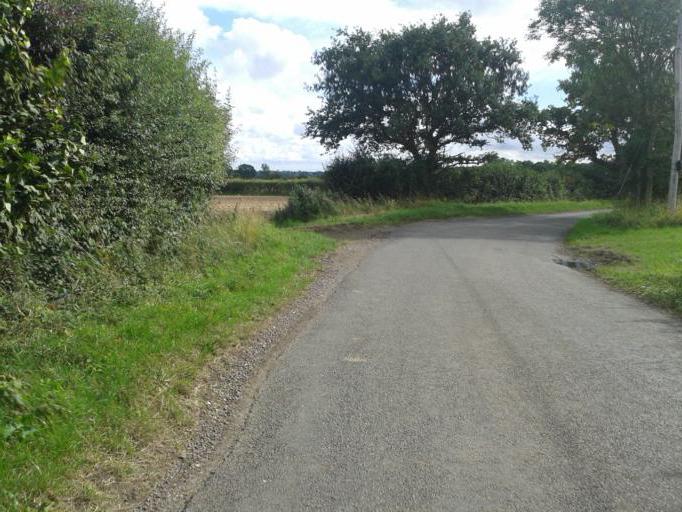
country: GB
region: England
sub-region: Hertfordshire
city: Reed
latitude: 51.9801
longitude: 0.0910
